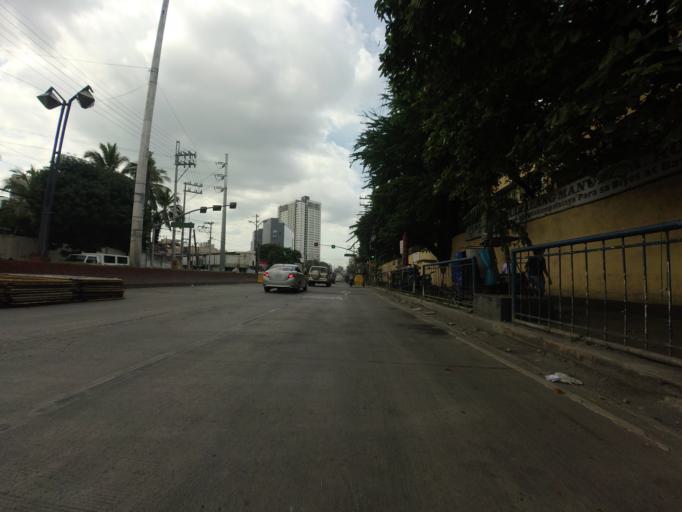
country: PH
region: Metro Manila
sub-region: City of Manila
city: Quiapo
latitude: 14.5817
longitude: 120.9985
